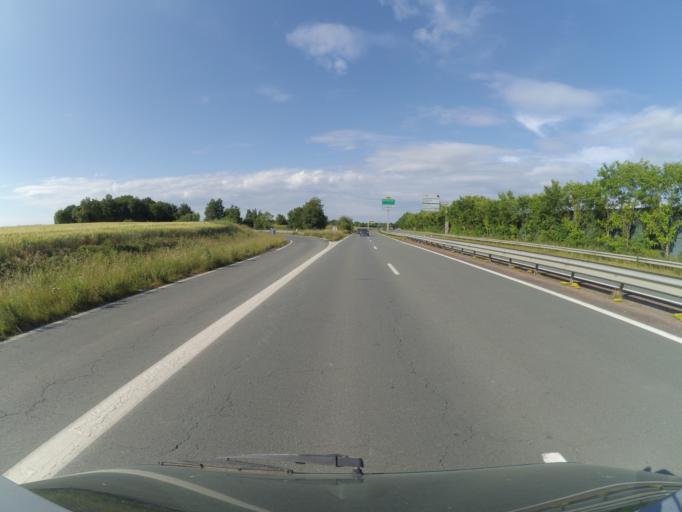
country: FR
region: Poitou-Charentes
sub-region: Departement de la Charente-Maritime
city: Saint-Agnant
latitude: 45.8770
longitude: -0.9662
